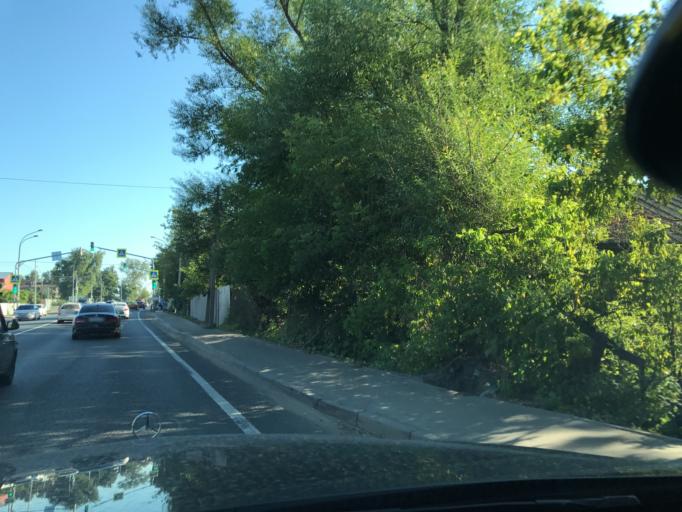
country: RU
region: Moskovskaya
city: Balashikha
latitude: 55.8359
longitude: 37.9458
